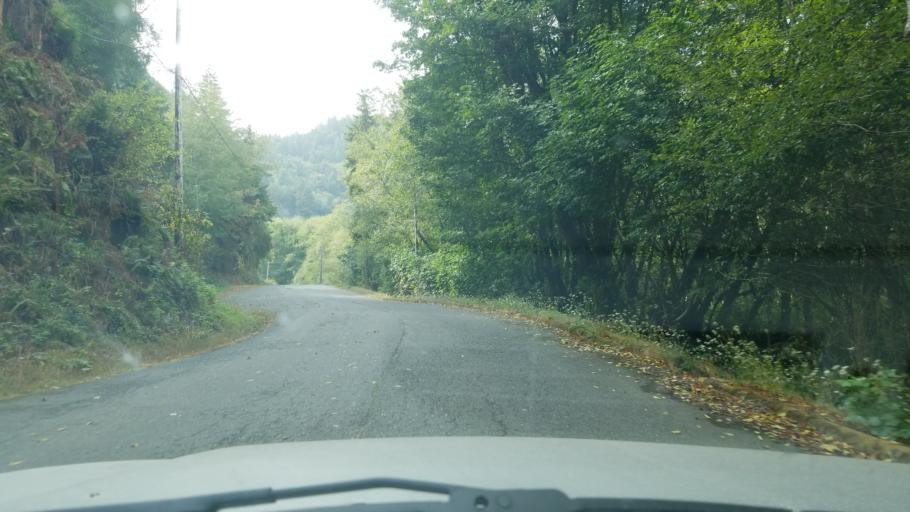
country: US
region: California
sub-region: Del Norte County
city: Bertsch-Oceanview
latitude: 41.5121
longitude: -124.0315
